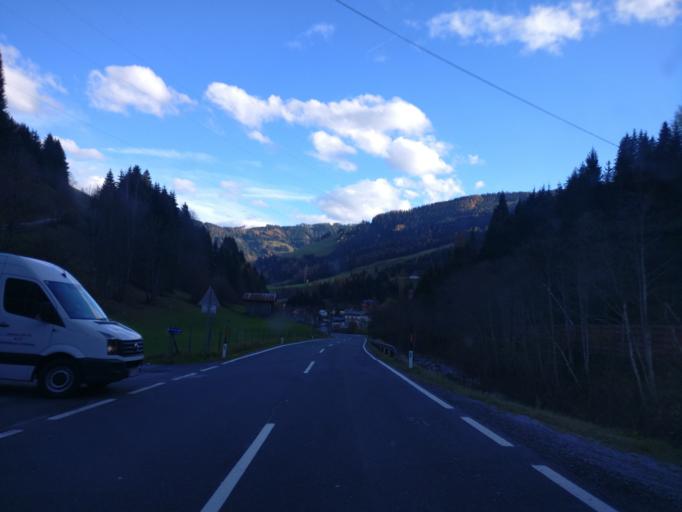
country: AT
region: Salzburg
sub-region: Politischer Bezirk Sankt Johann im Pongau
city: Muhlbach am Hochkonig
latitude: 47.3824
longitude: 13.1054
